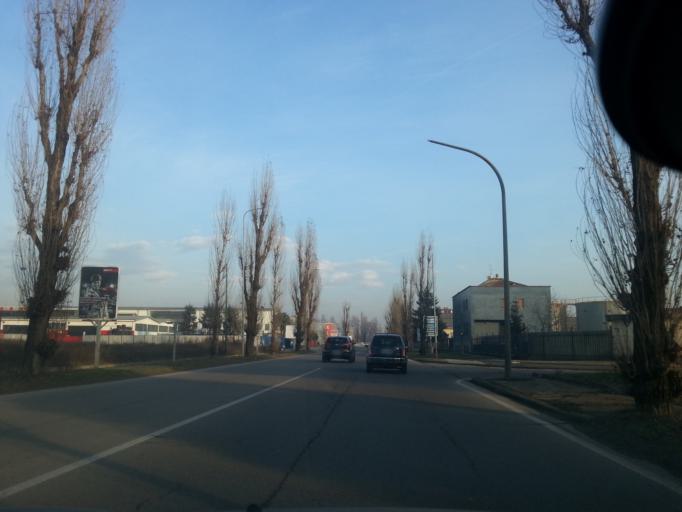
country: IT
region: Lombardy
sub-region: Citta metropolitana di Milano
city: Pero
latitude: 45.5285
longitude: 9.0828
